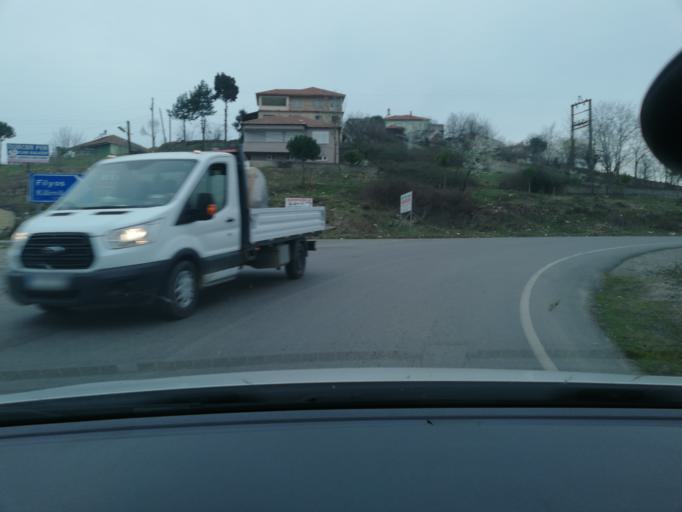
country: TR
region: Zonguldak
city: Saltukova
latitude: 41.5222
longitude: 32.0839
